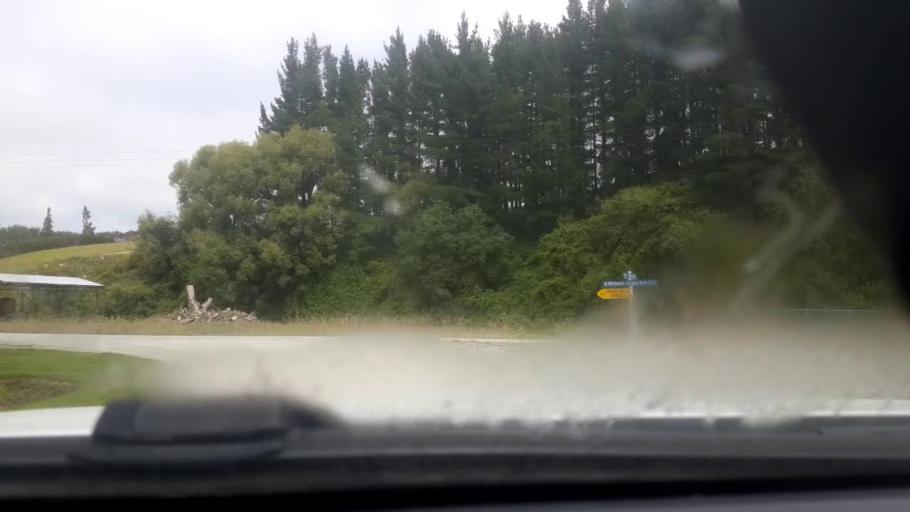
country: NZ
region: Canterbury
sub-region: Timaru District
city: Pleasant Point
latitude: -44.1882
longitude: 171.0536
